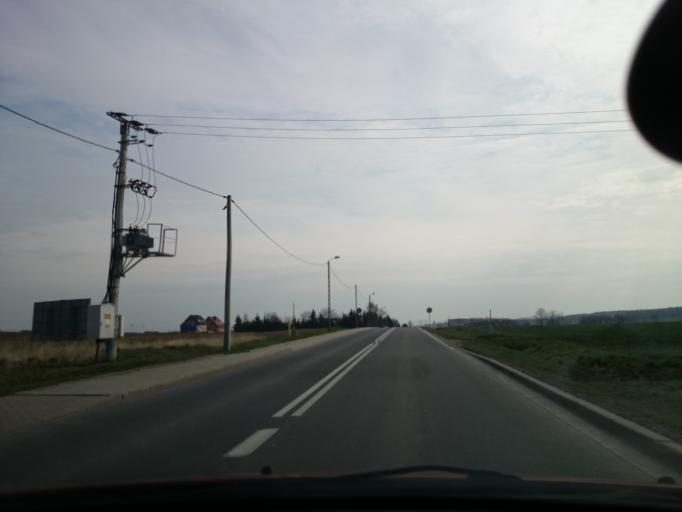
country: PL
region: Opole Voivodeship
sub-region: Powiat nyski
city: Glucholazy
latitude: 50.3173
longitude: 17.3987
